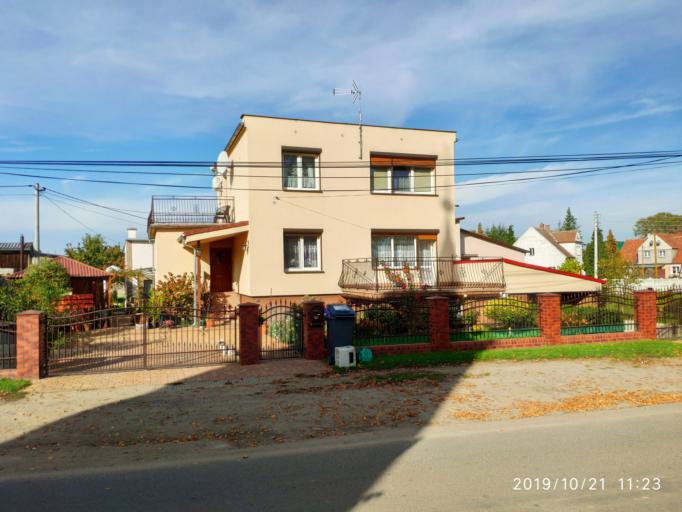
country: PL
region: Lubusz
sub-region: Powiat nowosolski
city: Otyn
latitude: 51.8649
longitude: 15.7299
